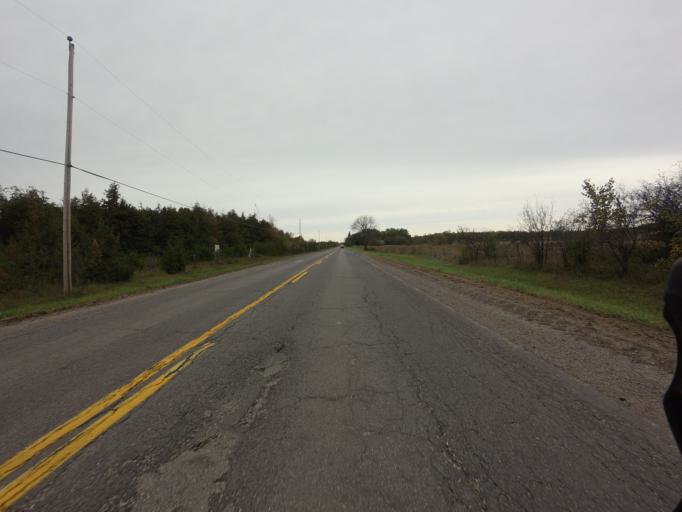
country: CA
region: Ontario
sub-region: Lanark County
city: Smiths Falls
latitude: 44.8763
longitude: -75.8136
